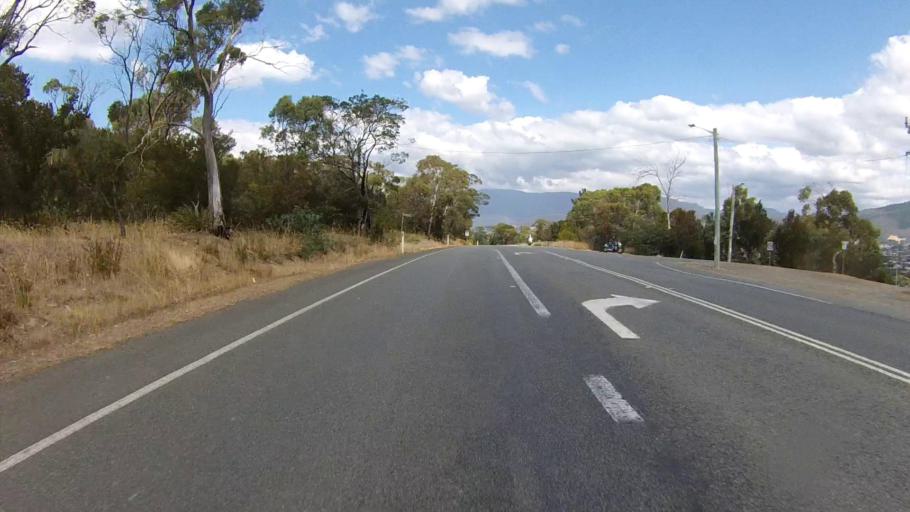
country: AU
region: Tasmania
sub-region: Brighton
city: Old Beach
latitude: -42.7708
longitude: 147.2691
